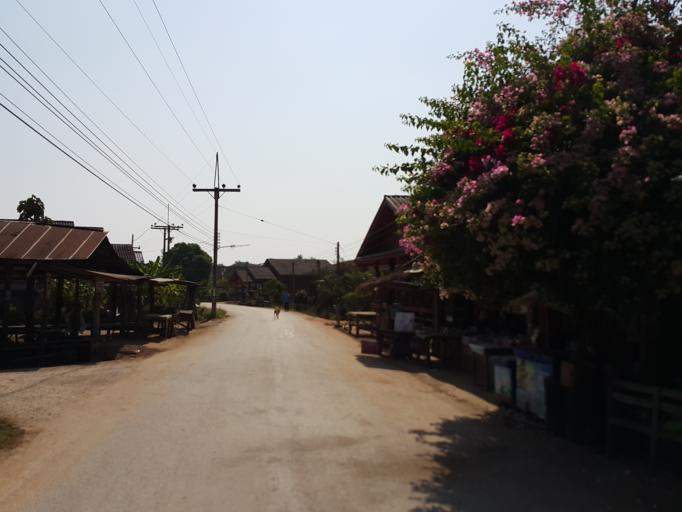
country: TH
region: Lampang
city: Wang Nuea
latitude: 19.0379
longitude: 99.6239
